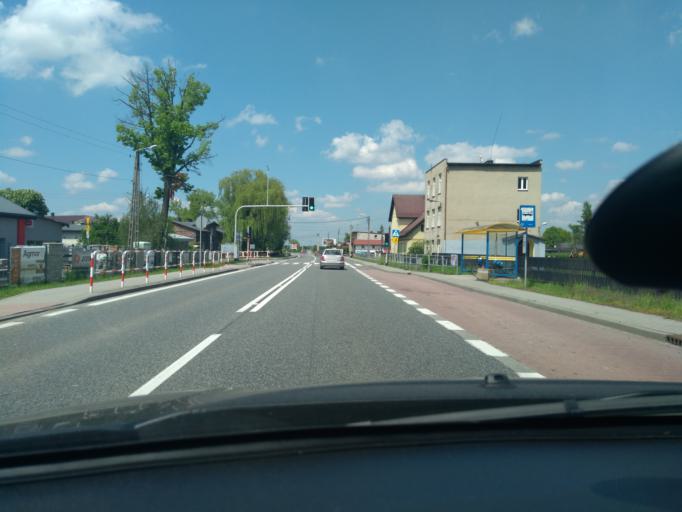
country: PL
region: Silesian Voivodeship
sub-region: Powiat mikolowski
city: Mikolow
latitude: 50.2002
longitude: 18.8623
